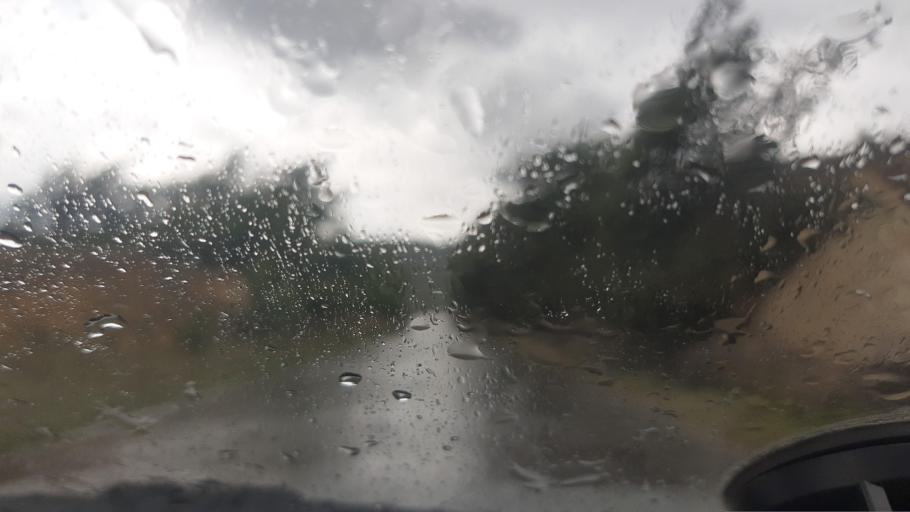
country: CO
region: Cundinamarca
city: Cucunuba
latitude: 5.1969
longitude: -73.7881
